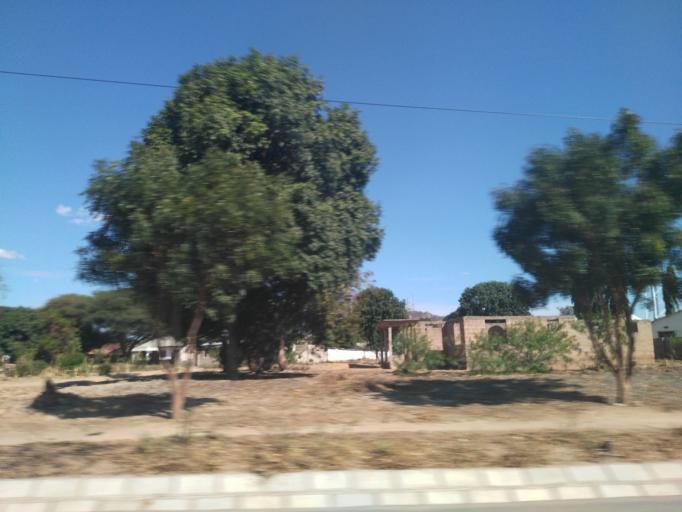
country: TZ
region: Dodoma
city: Dodoma
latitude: -6.1950
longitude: 35.7354
